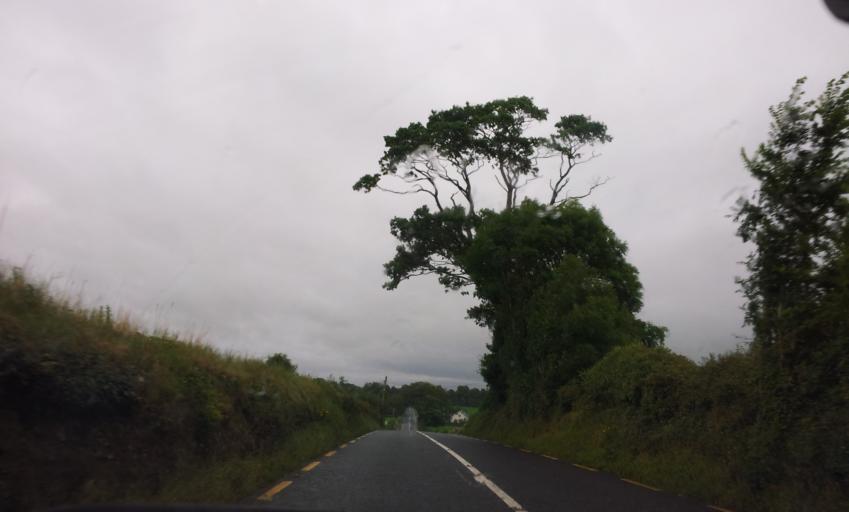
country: IE
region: Munster
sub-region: County Cork
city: Mitchelstown
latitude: 52.2624
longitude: -8.3136
